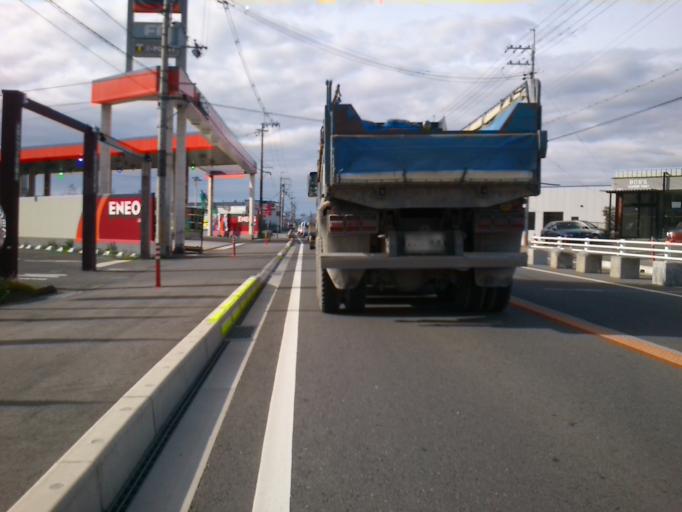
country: JP
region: Kyoto
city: Tanabe
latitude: 34.7638
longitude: 135.8097
